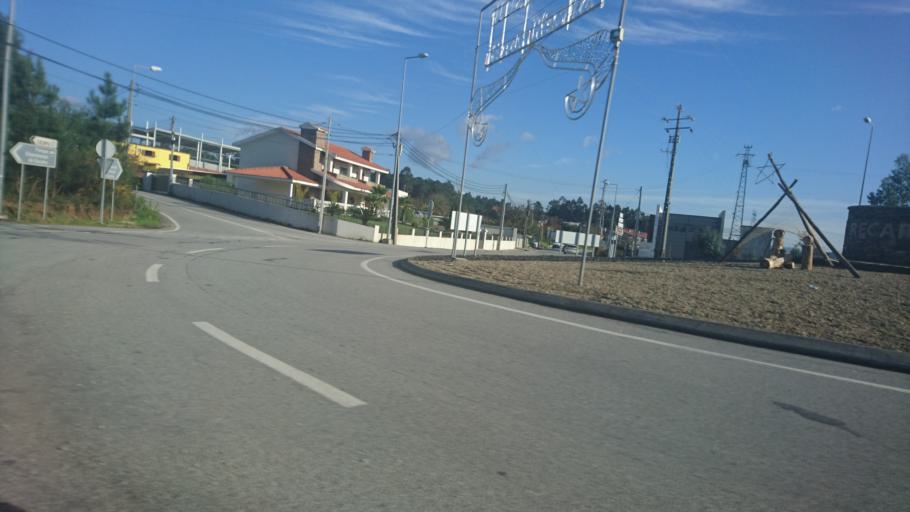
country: PT
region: Porto
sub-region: Valongo
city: Campo
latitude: 41.1714
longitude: -8.4407
